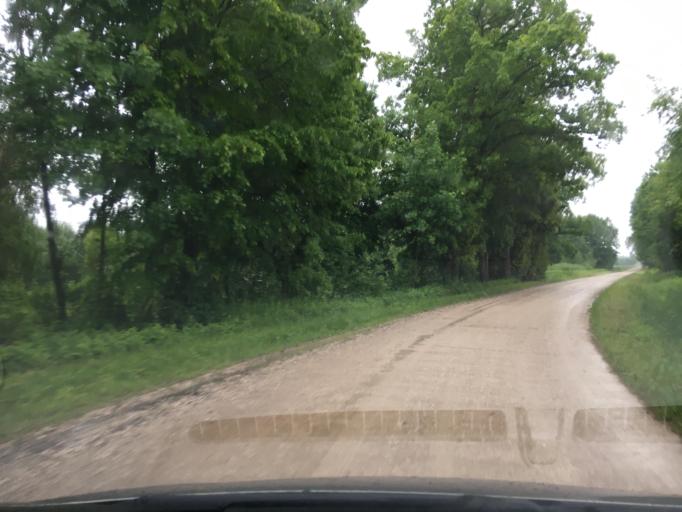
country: EE
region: Laeaene
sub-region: Lihula vald
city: Lihula
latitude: 58.6301
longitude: 23.8141
